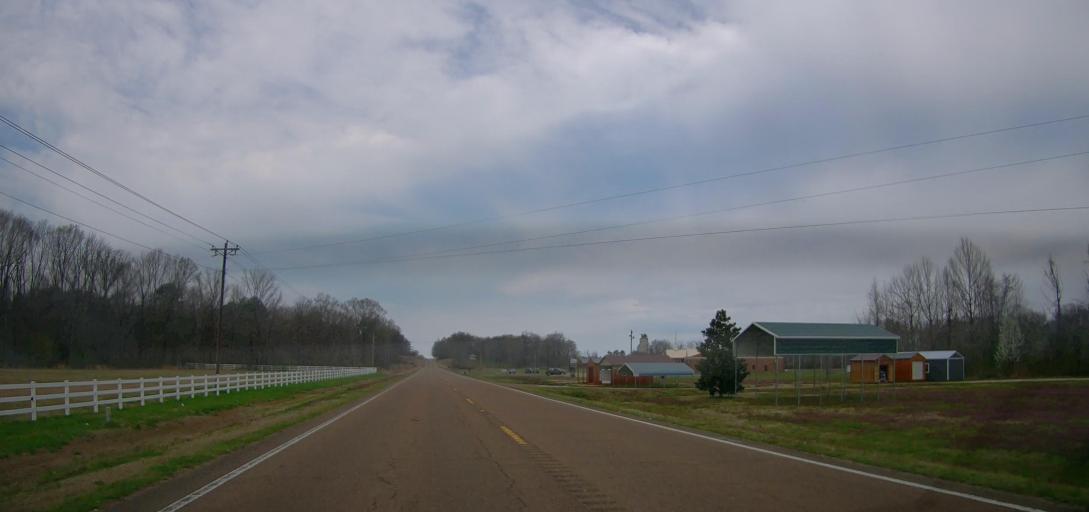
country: US
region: Mississippi
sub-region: Marshall County
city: Byhalia
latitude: 34.8564
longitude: -89.6448
